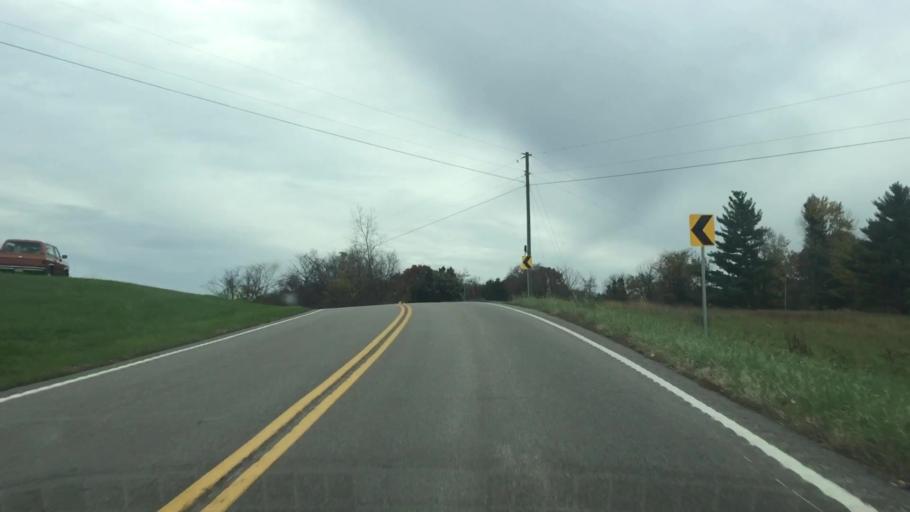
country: US
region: Missouri
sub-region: Callaway County
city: Fulton
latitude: 38.7124
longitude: -91.7358
